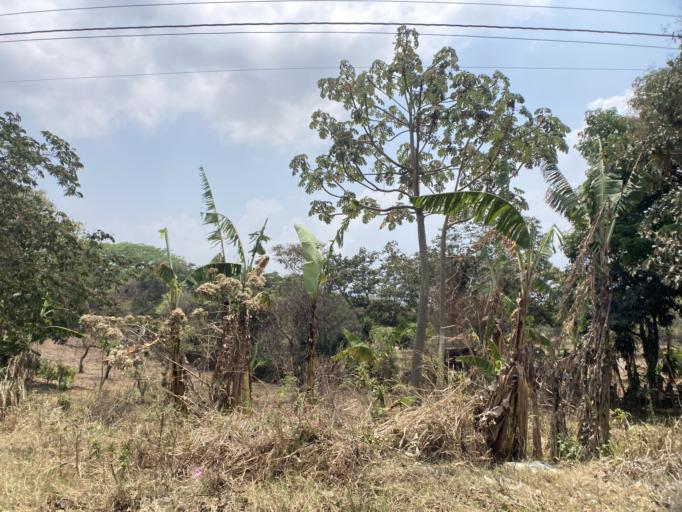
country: GT
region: Santa Rosa
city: Pueblo Nuevo Vinas
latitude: 14.3309
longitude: -90.5210
